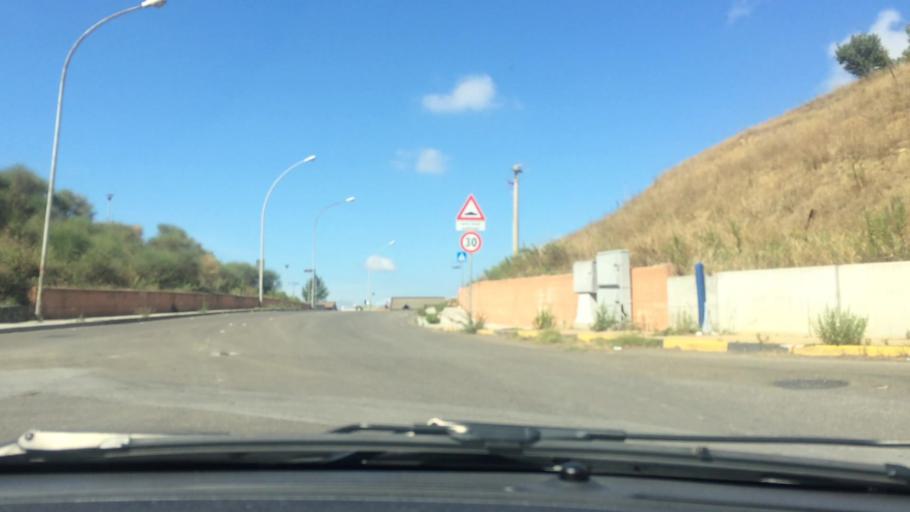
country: IT
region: Basilicate
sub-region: Provincia di Matera
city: Montescaglioso
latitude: 40.5446
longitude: 16.6686
